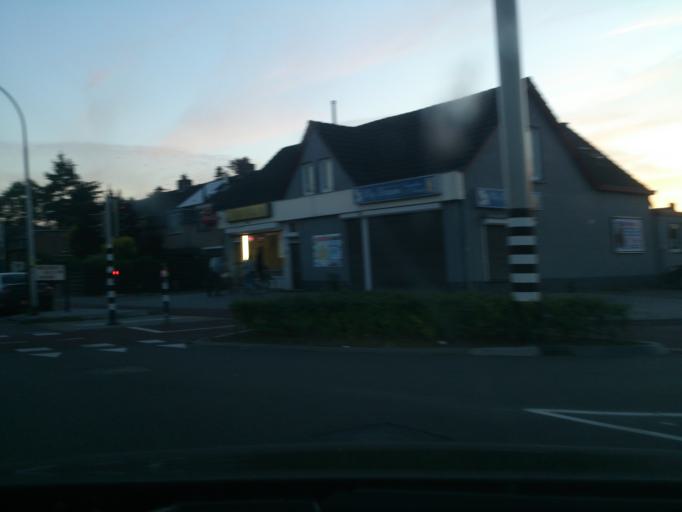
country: NL
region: Gelderland
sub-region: Gemeente Nijmegen
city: Nijmegen
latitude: 51.8112
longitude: 5.8309
